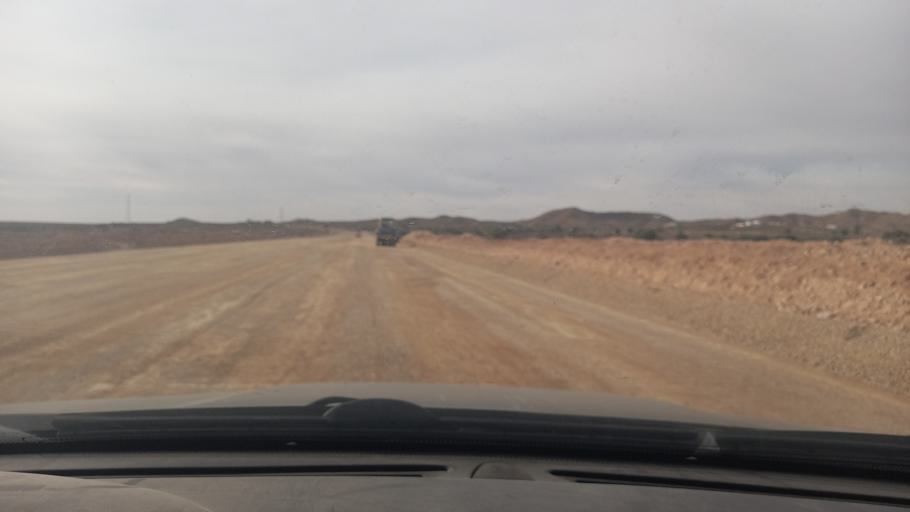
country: TN
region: Tataouine
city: Tataouine
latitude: 33.1279
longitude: 10.4995
